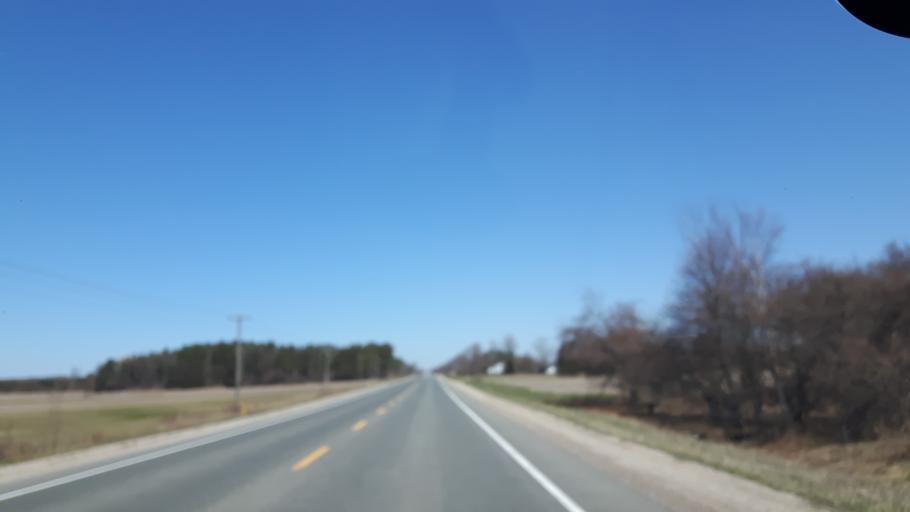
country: CA
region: Ontario
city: Goderich
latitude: 43.7039
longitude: -81.7056
